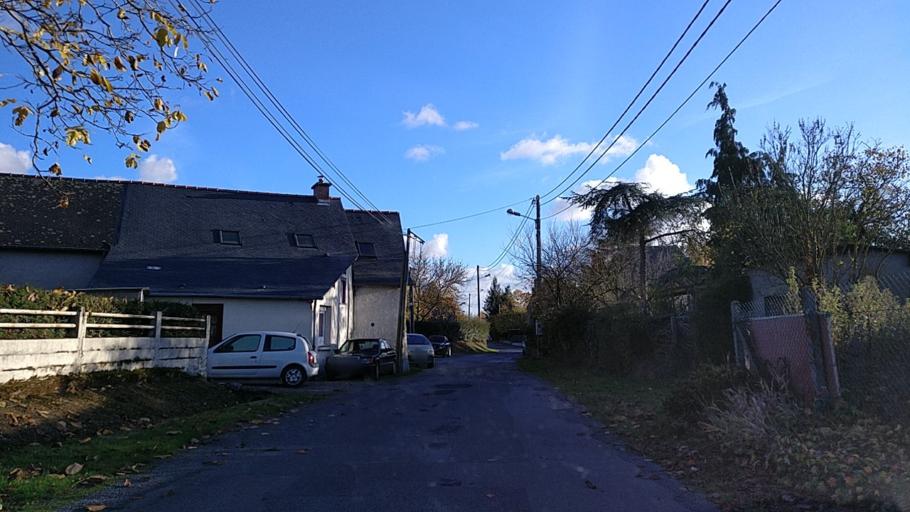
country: FR
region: Brittany
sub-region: Departement d'Ille-et-Vilaine
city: Fouillard
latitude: 48.1364
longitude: -1.5699
